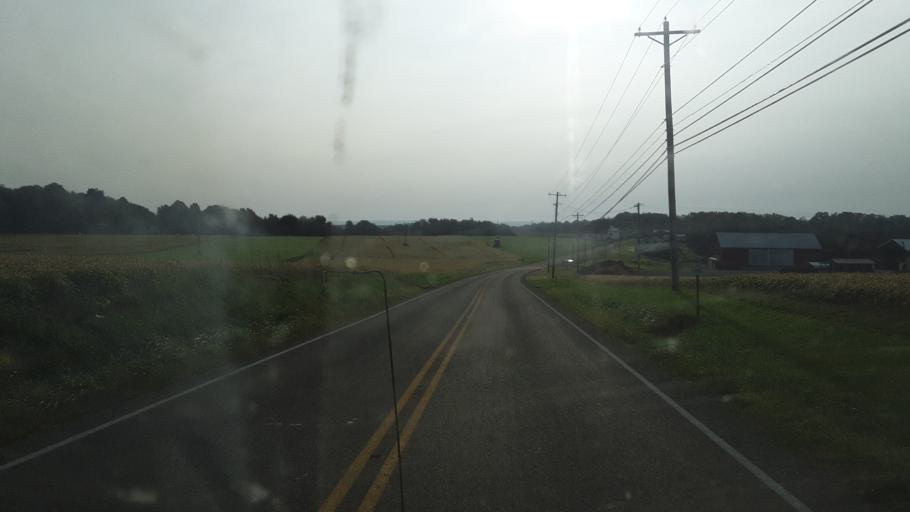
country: US
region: Pennsylvania
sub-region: Jefferson County
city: Punxsutawney
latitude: 40.9633
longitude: -79.0887
